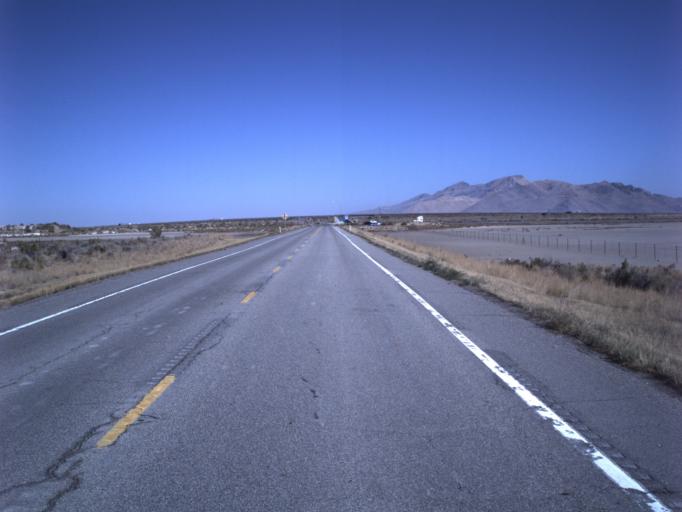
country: US
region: Utah
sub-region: Tooele County
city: Grantsville
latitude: 40.7006
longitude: -112.5298
